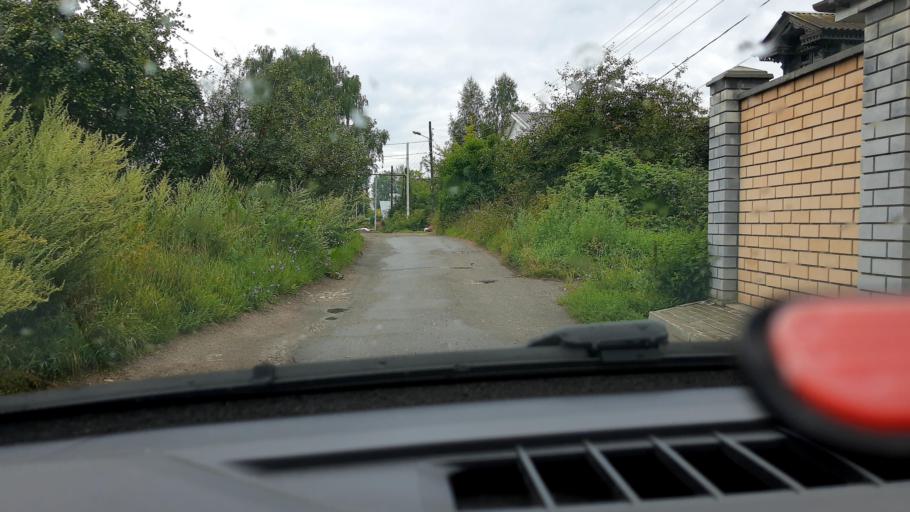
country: RU
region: Nizjnij Novgorod
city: Gorbatovka
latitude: 56.3759
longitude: 43.8266
